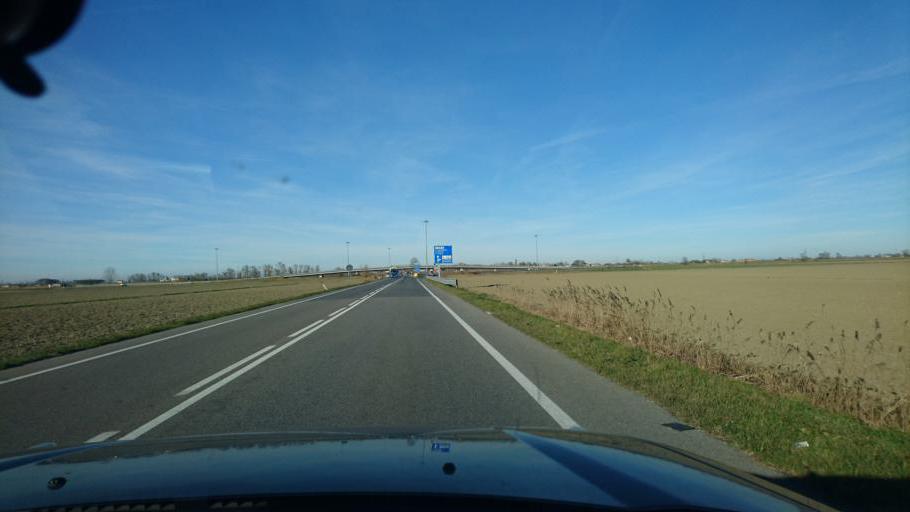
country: IT
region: Veneto
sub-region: Provincia di Rovigo
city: Bottrighe
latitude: 45.0355
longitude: 12.1000
